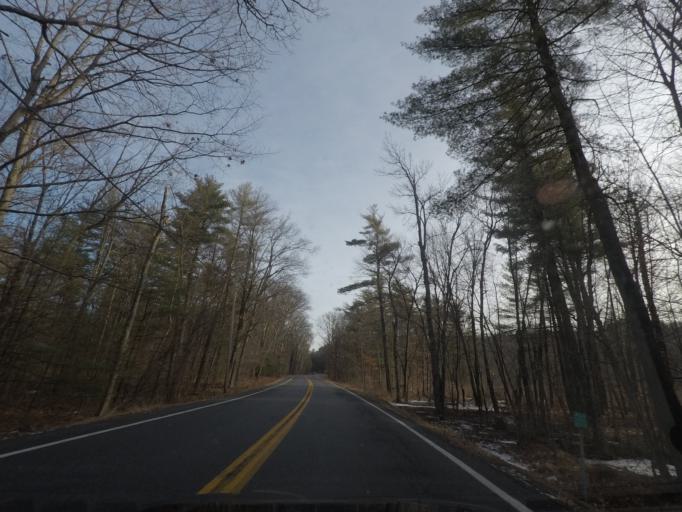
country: US
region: New York
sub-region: Saratoga County
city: Stillwater
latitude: 42.9910
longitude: -73.7101
